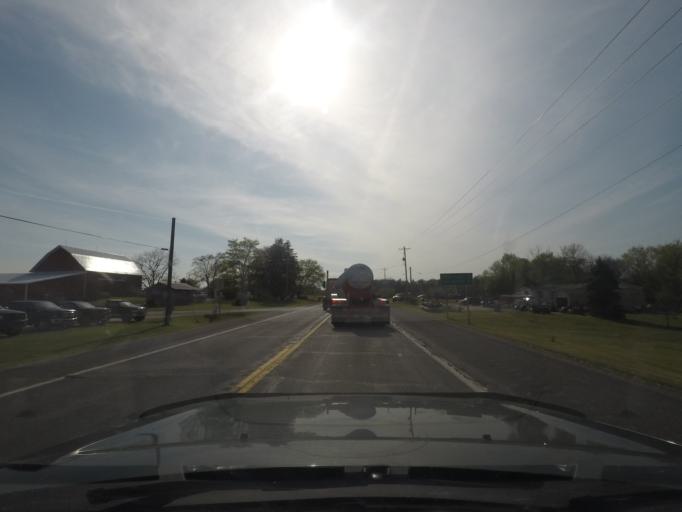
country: US
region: Indiana
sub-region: LaPorte County
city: Hudson Lake
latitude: 41.7981
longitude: -86.5043
